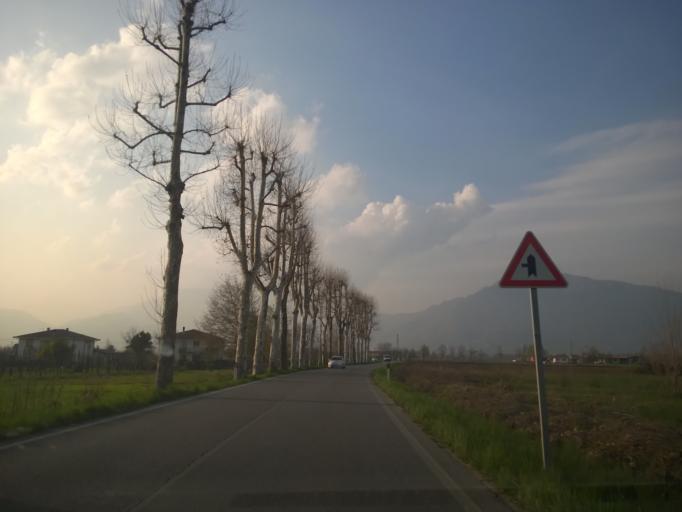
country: IT
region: Veneto
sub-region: Provincia di Vicenza
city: Giavenale
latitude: 45.6978
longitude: 11.4116
